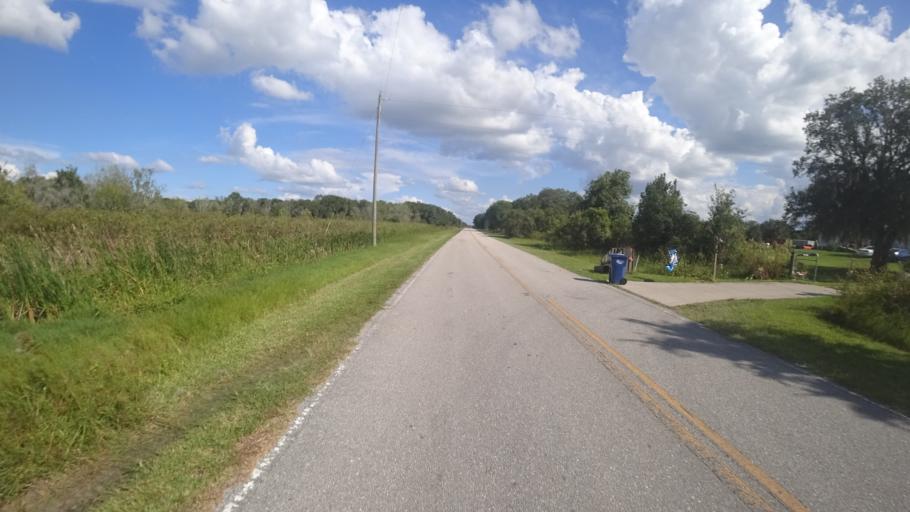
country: US
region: Florida
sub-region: DeSoto County
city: Nocatee
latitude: 27.2735
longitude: -82.1088
